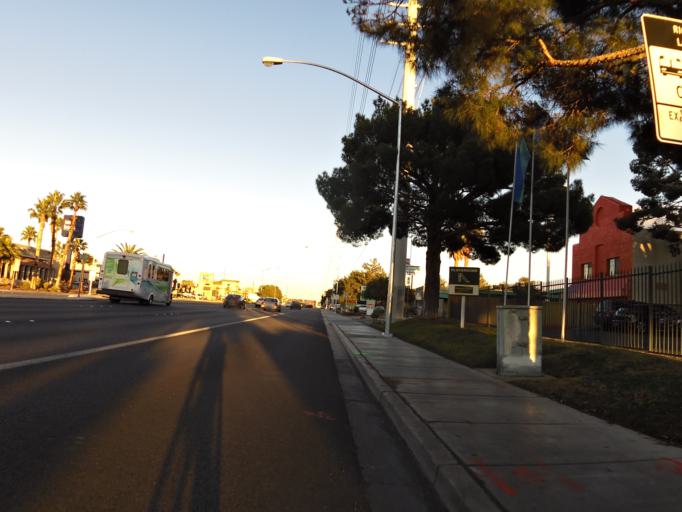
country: US
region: Nevada
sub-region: Clark County
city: Spring Valley
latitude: 36.1145
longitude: -115.2232
